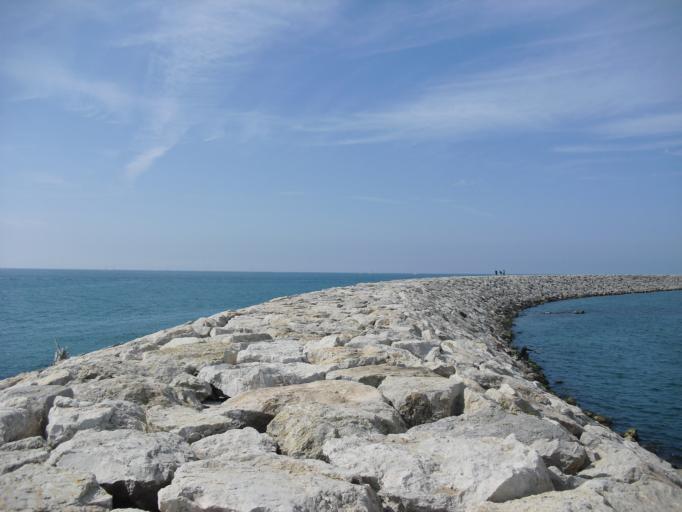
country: ES
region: Catalonia
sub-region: Provincia de Barcelona
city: Vilanova i la Geltru
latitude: 41.2094
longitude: 1.7341
